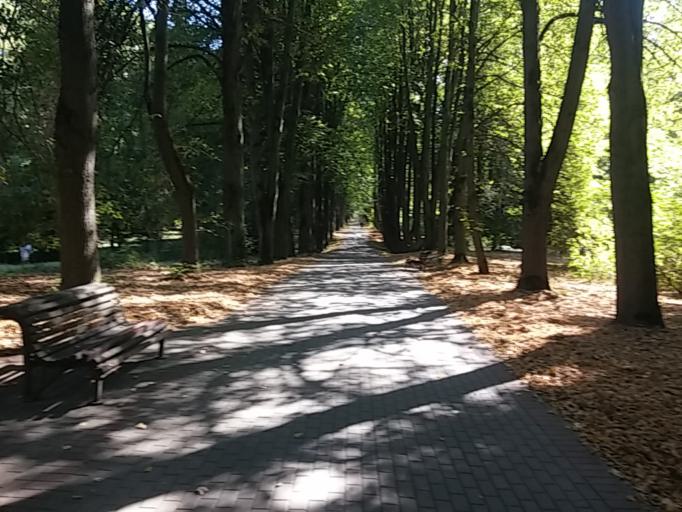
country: BY
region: Minsk
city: Minsk
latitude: 53.9147
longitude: 27.6127
